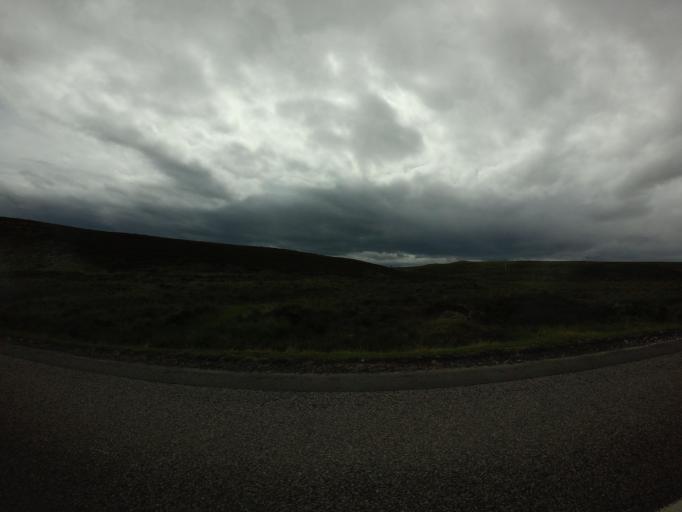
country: GB
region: Scotland
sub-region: Highland
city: Dingwall
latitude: 57.6922
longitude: -4.7478
